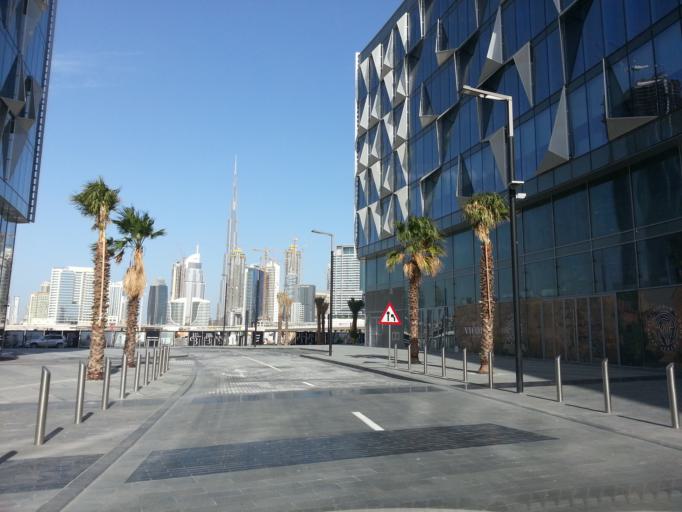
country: AE
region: Dubai
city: Dubai
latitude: 25.1879
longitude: 55.2974
